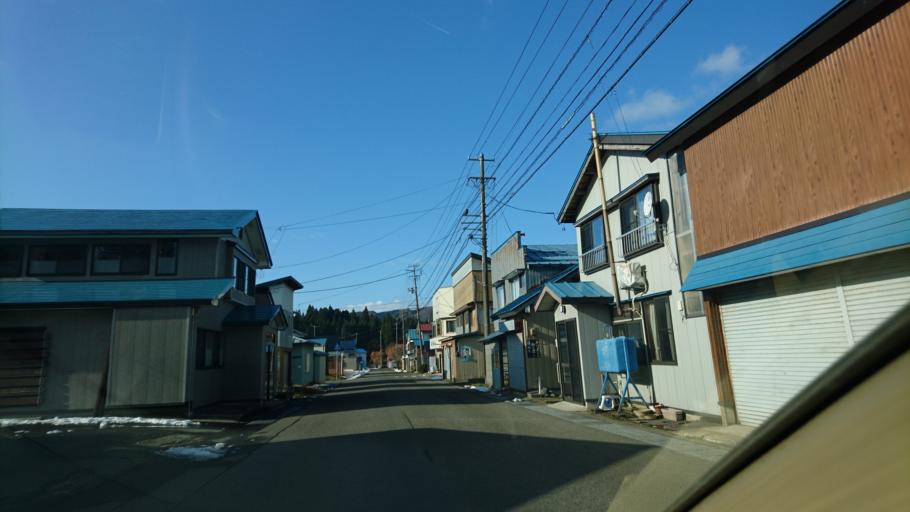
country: JP
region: Iwate
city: Kitakami
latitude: 39.2955
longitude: 140.8366
